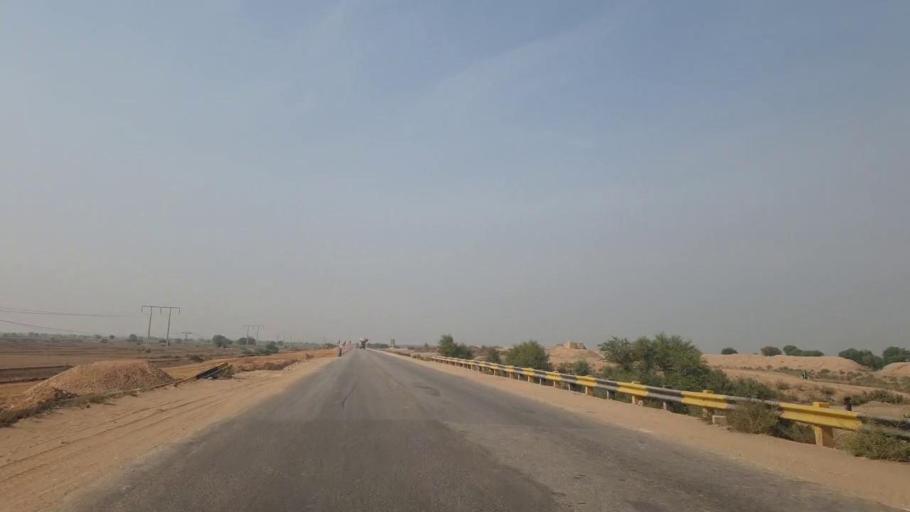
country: PK
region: Sindh
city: Sann
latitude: 26.1418
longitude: 68.0375
